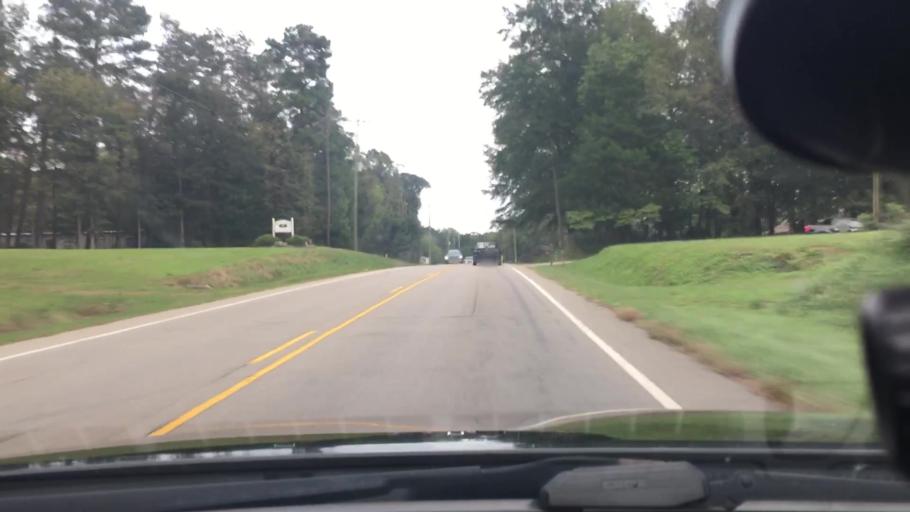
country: US
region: North Carolina
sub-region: Moore County
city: Robbins
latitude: 35.4037
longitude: -79.5642
